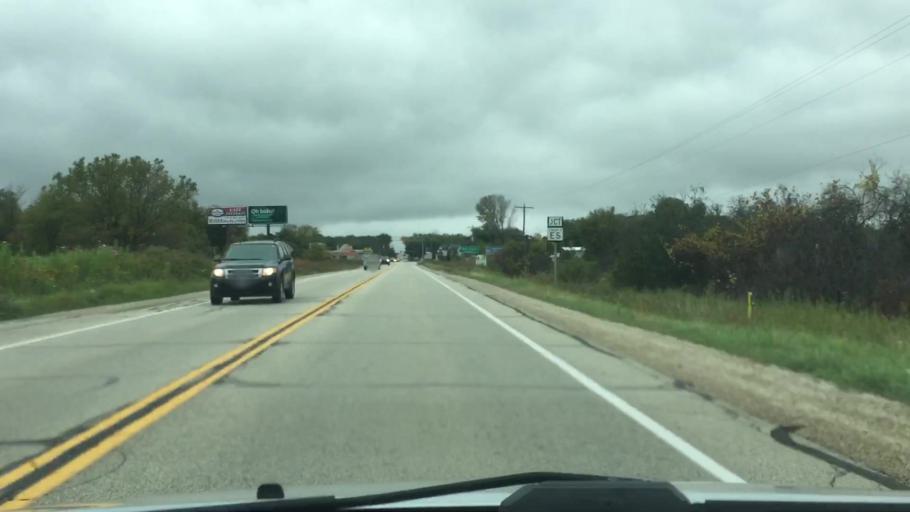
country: US
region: Wisconsin
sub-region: Walworth County
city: Elkhorn
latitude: 42.7293
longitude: -88.5429
